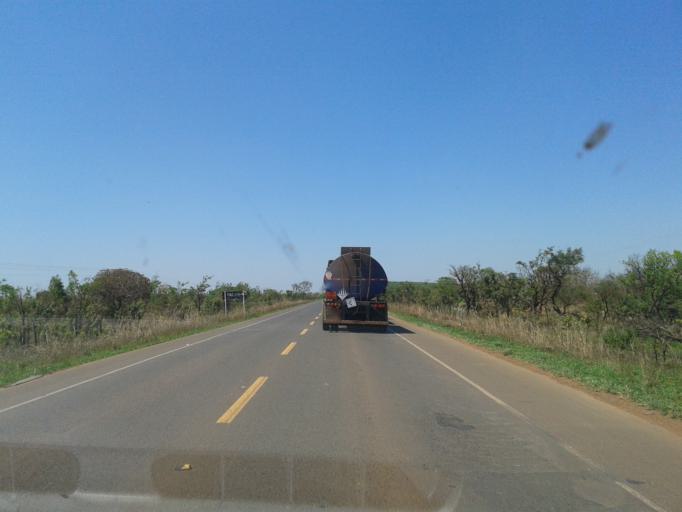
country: BR
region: Minas Gerais
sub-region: Araxa
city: Araxa
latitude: -19.3208
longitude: -47.3846
